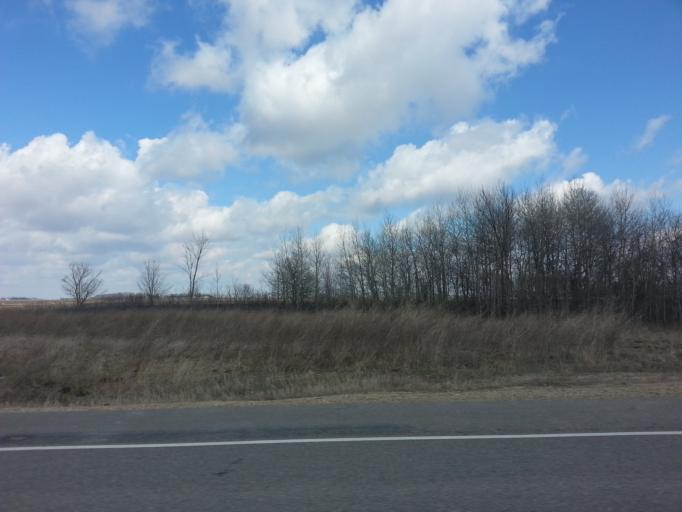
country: US
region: Minnesota
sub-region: Goodhue County
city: Kenyon
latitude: 44.2423
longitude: -92.9607
